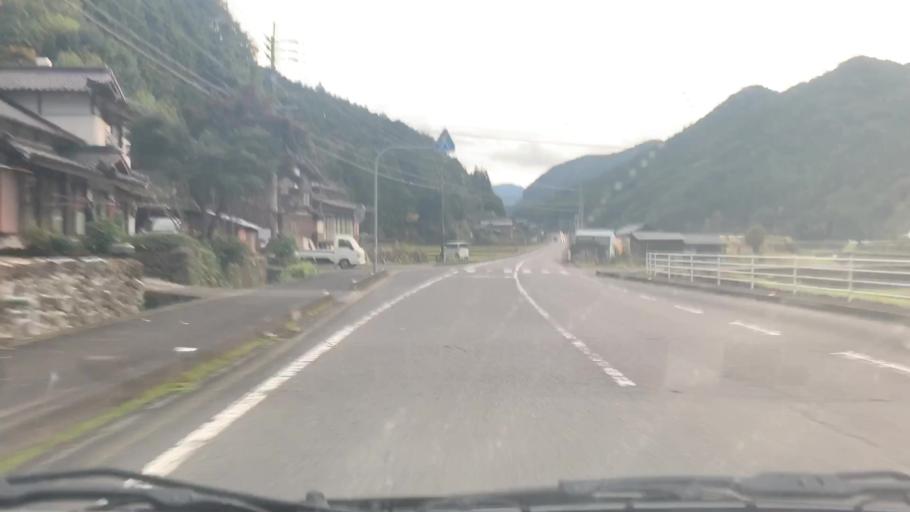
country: JP
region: Saga Prefecture
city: Kashima
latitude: 33.0648
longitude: 130.0705
